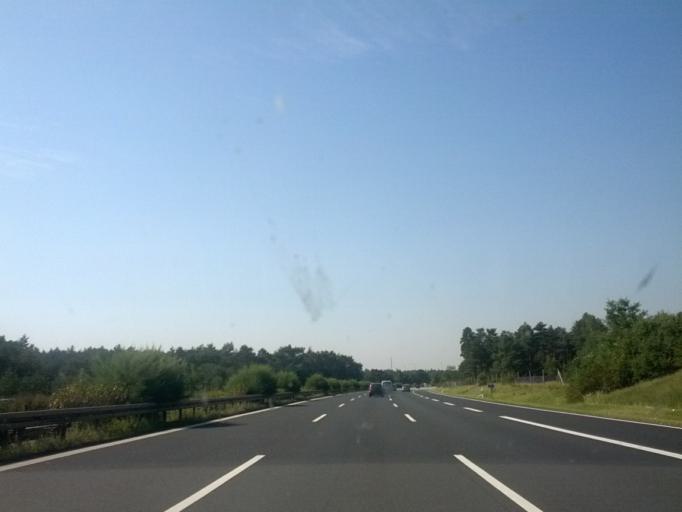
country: DE
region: Brandenburg
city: Borkheide
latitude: 52.1999
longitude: 12.8825
